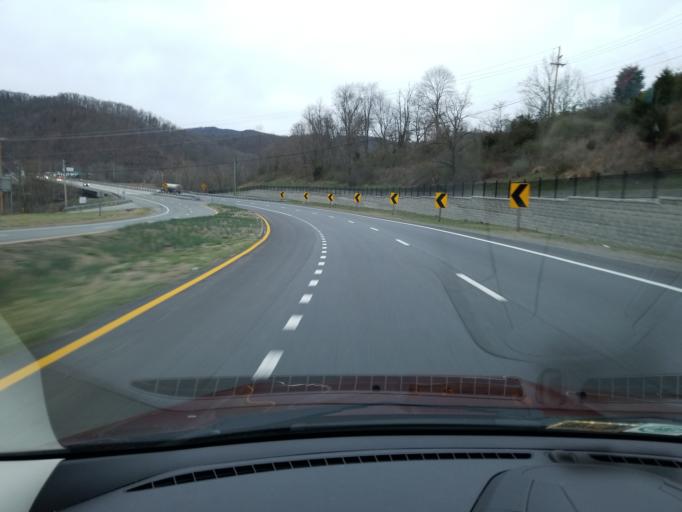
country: US
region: Virginia
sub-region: Giles County
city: Narrows
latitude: 37.3736
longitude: -80.8584
